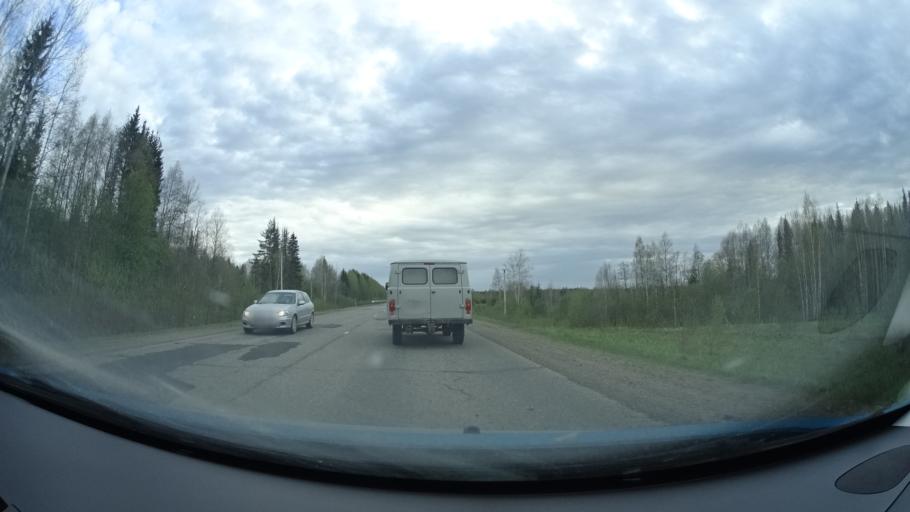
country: RU
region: Perm
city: Osa
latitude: 57.4446
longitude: 55.6420
